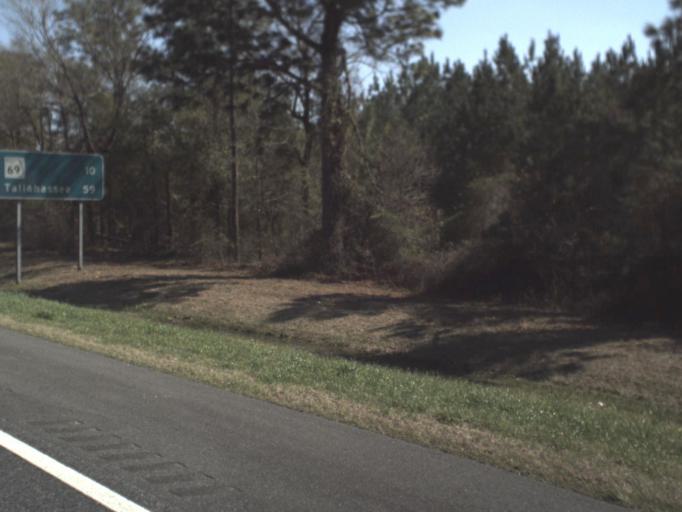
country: US
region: Florida
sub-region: Jackson County
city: Marianna
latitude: 30.7179
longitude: -85.1696
